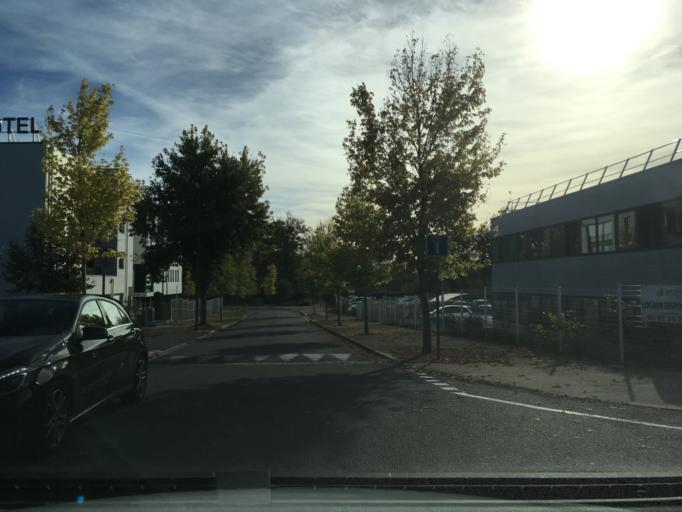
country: FR
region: Aquitaine
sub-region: Departement des Pyrenees-Atlantiques
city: Pau
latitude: 43.3297
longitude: -0.3585
